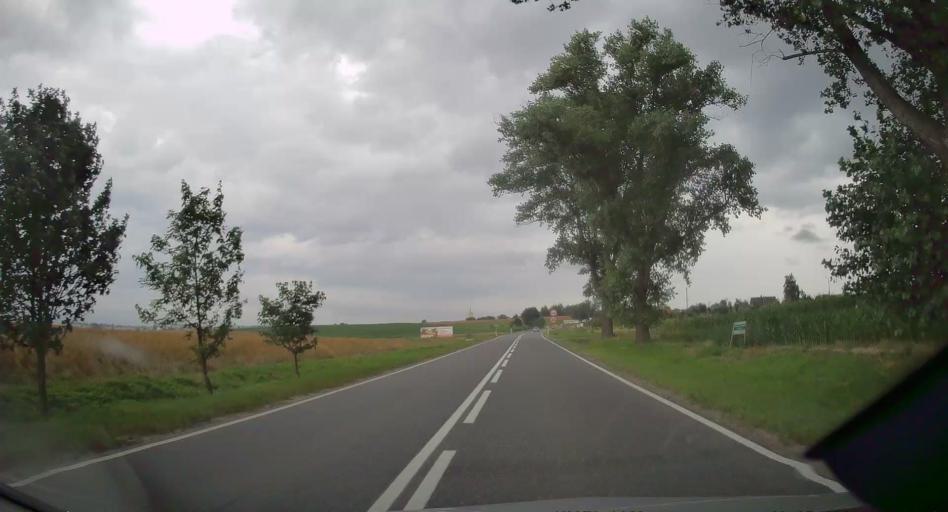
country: PL
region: Opole Voivodeship
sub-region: Powiat nyski
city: Nysa
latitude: 50.4229
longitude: 17.4440
